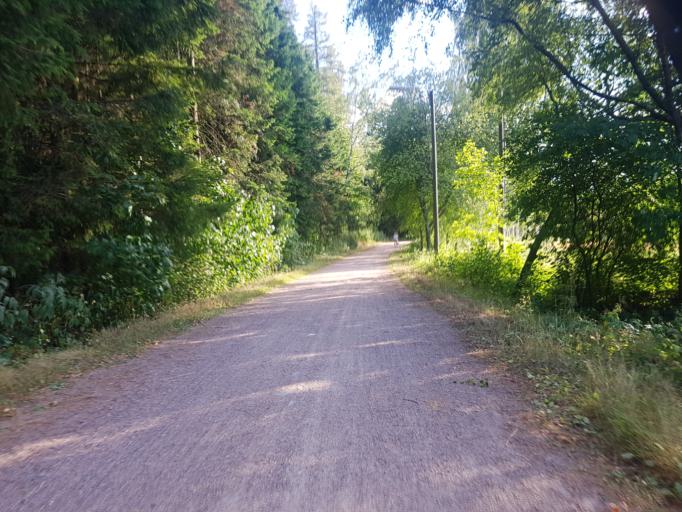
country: FI
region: Uusimaa
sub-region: Helsinki
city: Vantaa
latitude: 60.2534
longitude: 24.9664
